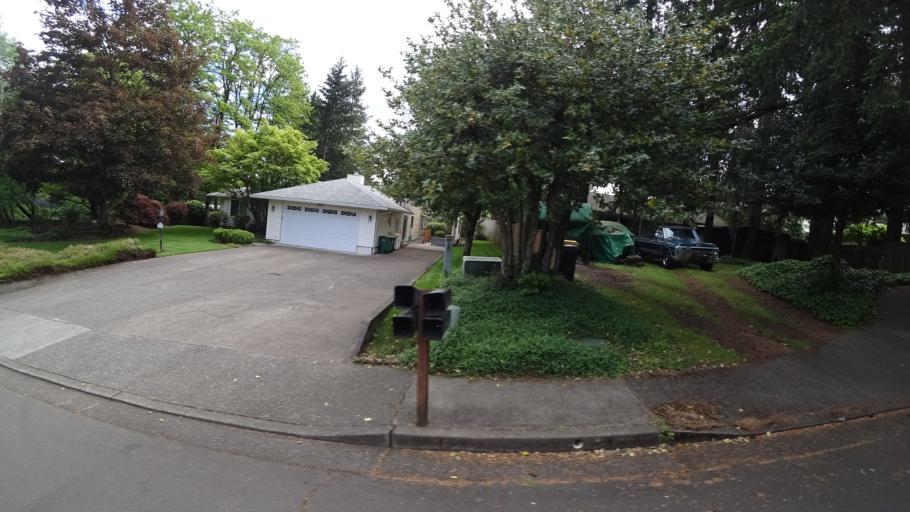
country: US
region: Oregon
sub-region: Washington County
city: Beaverton
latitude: 45.4654
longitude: -122.8120
